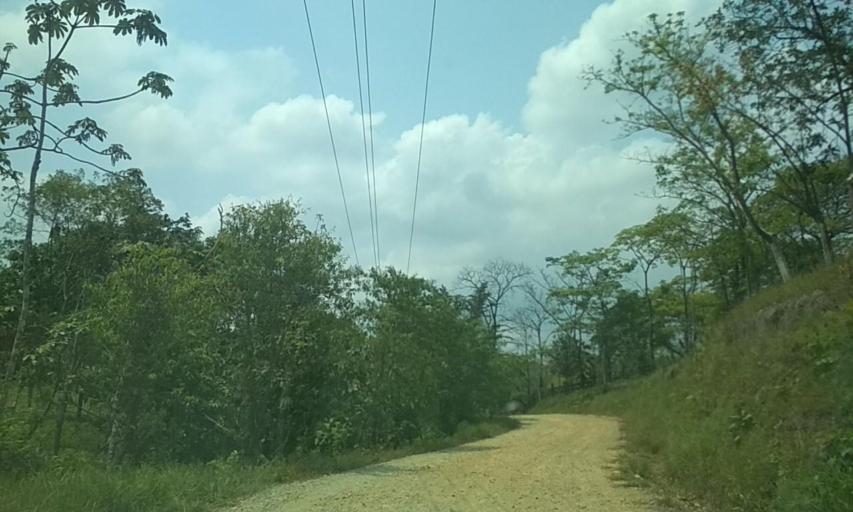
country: MX
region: Tabasco
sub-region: Huimanguillo
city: Francisco Rueda
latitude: 17.6150
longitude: -93.8129
